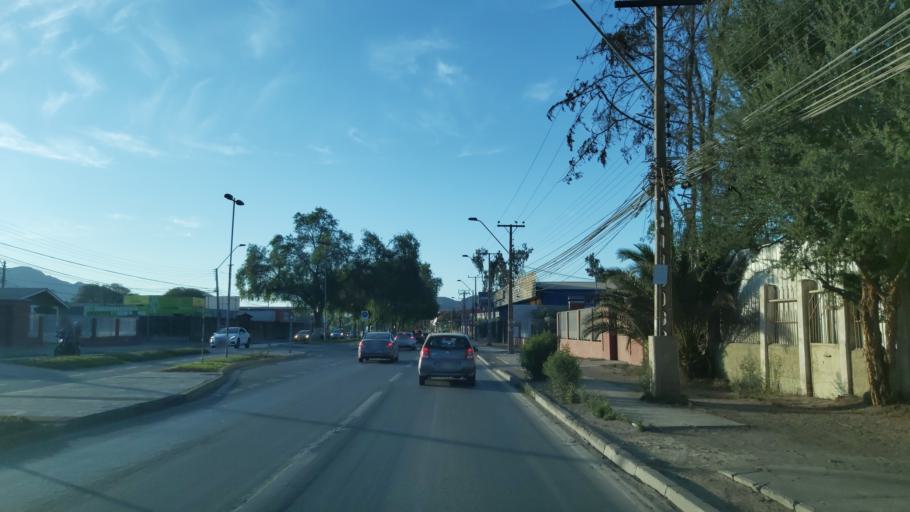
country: CL
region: Atacama
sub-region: Provincia de Copiapo
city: Copiapo
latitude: -27.3801
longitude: -70.3180
